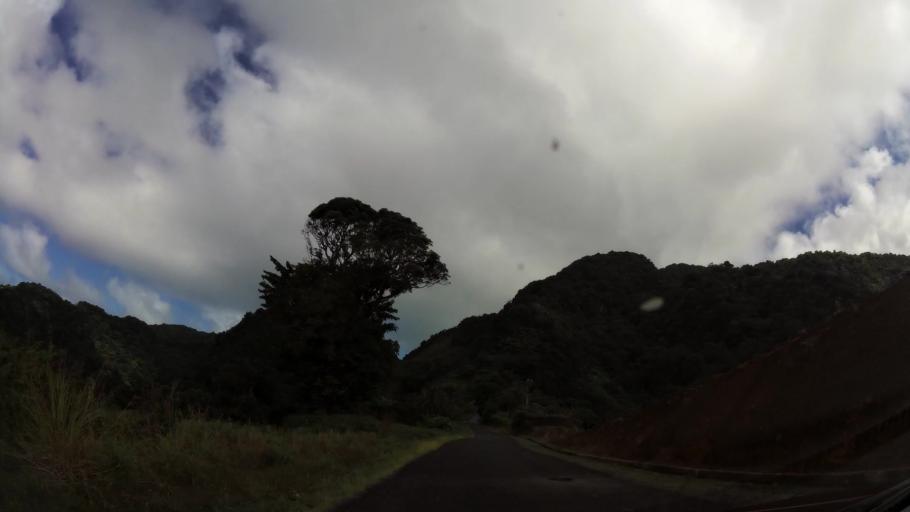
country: DM
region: Saint John
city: Portsmouth
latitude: 15.6141
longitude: -61.4475
